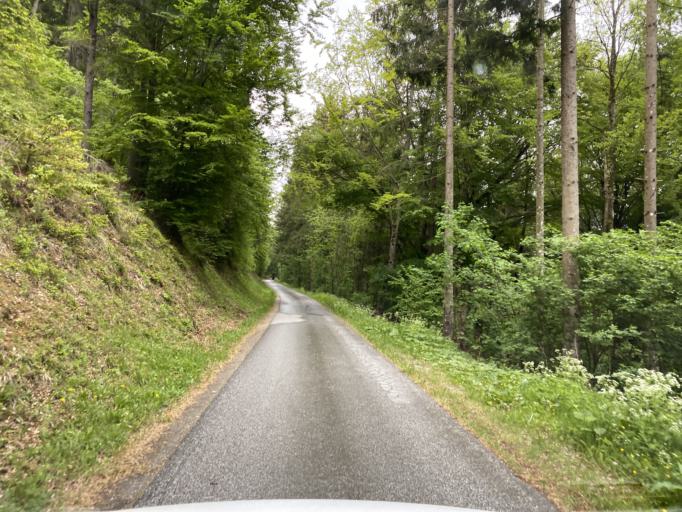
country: AT
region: Styria
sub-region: Politischer Bezirk Weiz
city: Koglhof
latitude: 47.3323
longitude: 15.6675
